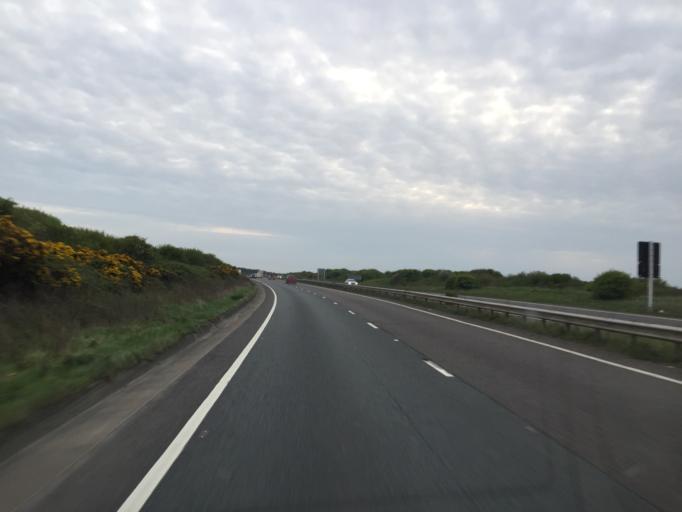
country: GB
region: England
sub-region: Kent
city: Dover
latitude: 51.1069
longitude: 1.2631
